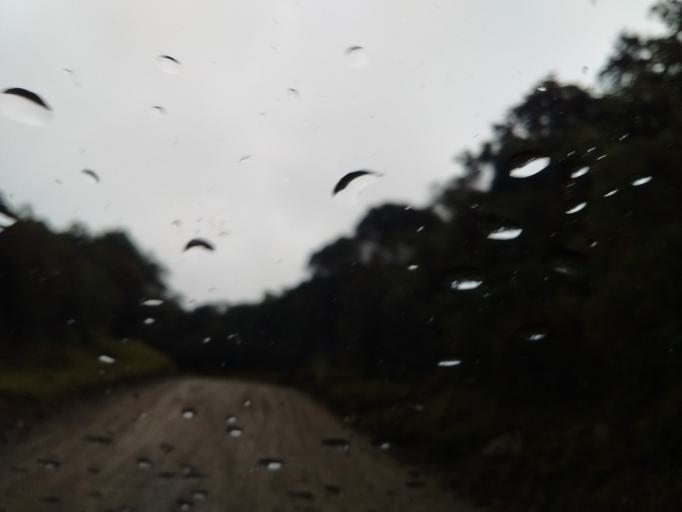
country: CO
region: Cauca
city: Paispamba
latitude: 2.1649
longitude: -76.3997
